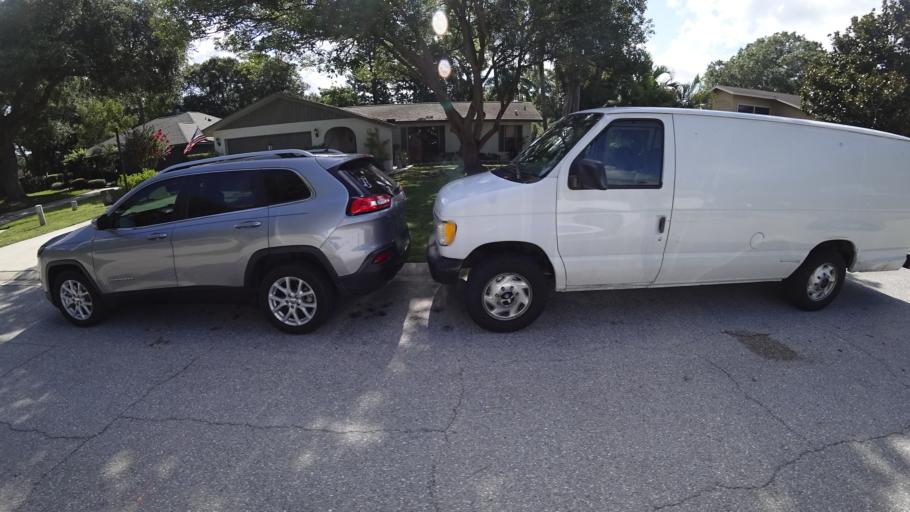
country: US
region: Florida
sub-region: Sarasota County
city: Desoto Lakes
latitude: 27.3992
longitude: -82.5010
